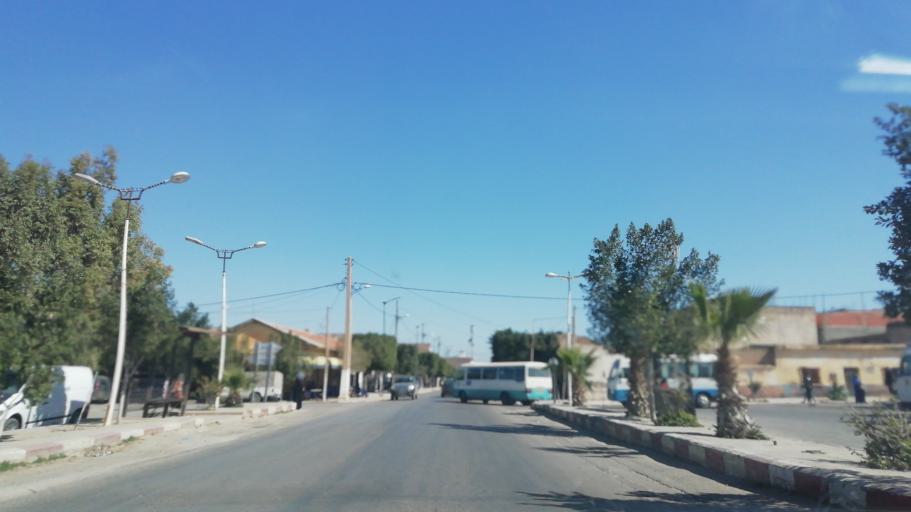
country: DZ
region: Mascara
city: Sig
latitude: 35.5623
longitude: -0.0925
